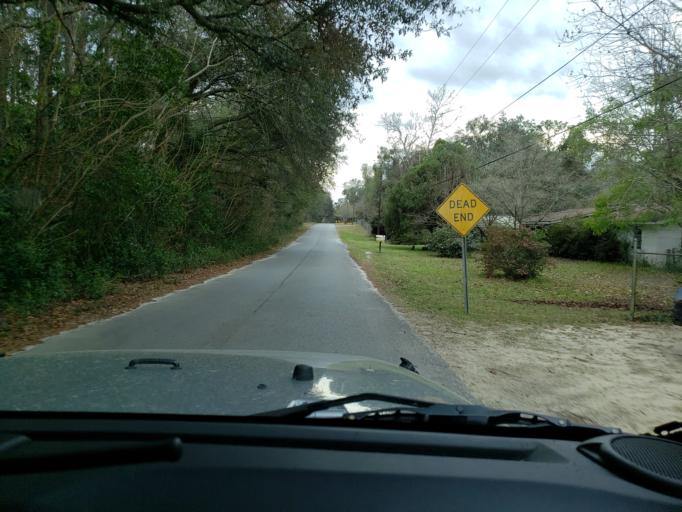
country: US
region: Georgia
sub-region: Chatham County
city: Bloomingdale
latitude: 32.0772
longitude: -81.3694
